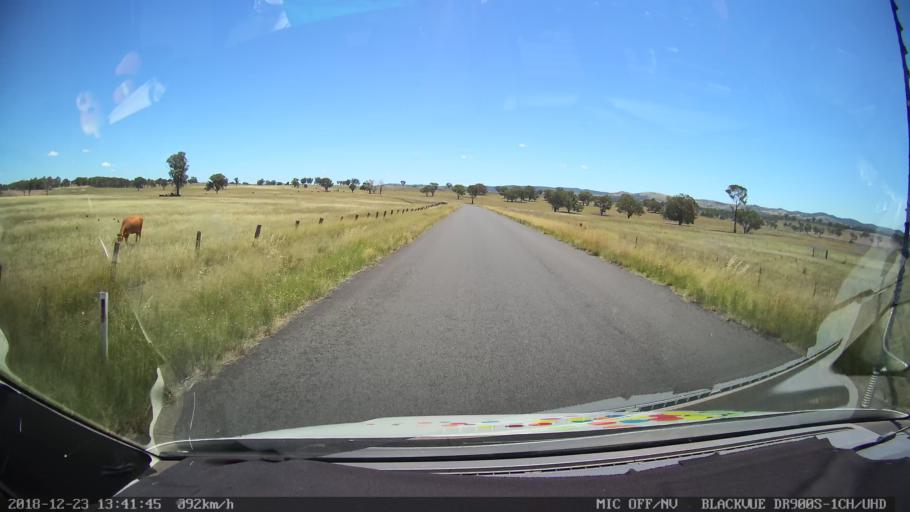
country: AU
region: New South Wales
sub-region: Armidale Dumaresq
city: Armidale
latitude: -30.4706
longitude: 151.1713
